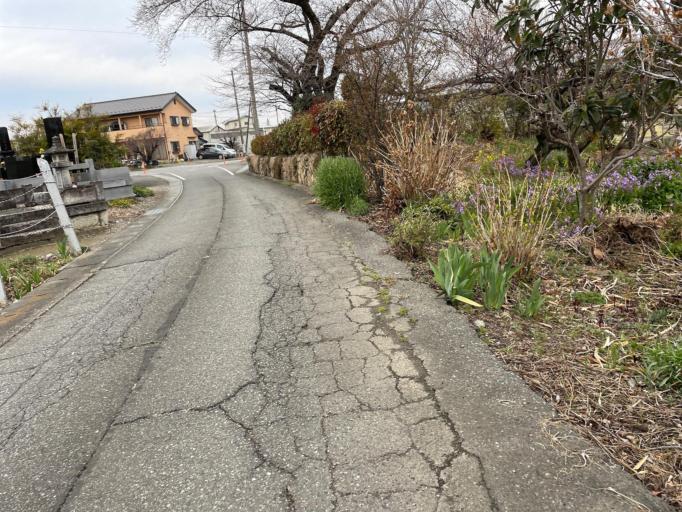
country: JP
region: Gunma
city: Fujioka
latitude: 36.2398
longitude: 139.0920
